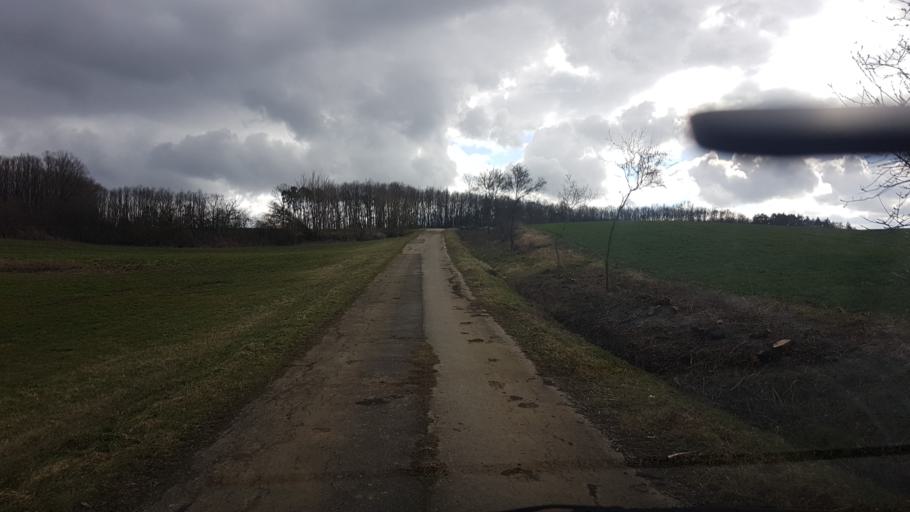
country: DE
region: Bavaria
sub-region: Upper Franconia
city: Hirschaid
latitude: 49.7931
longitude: 10.9728
